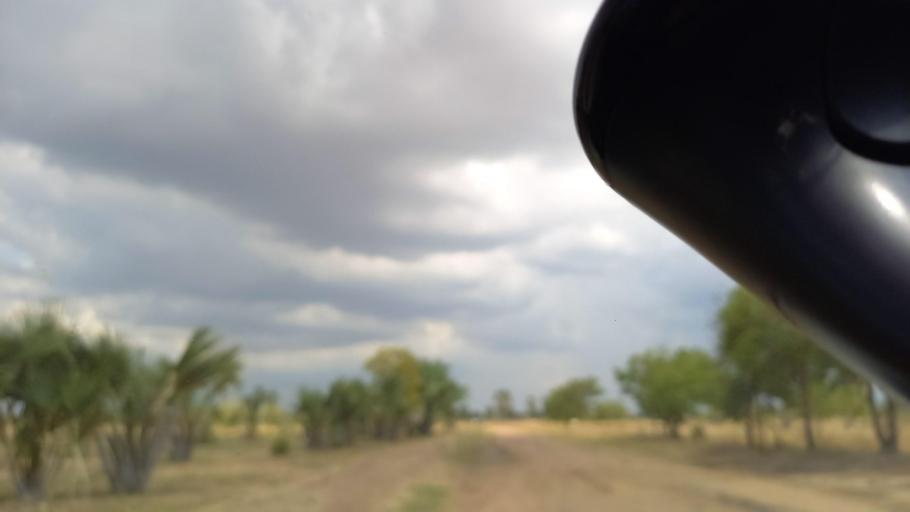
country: ZM
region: Lusaka
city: Kafue
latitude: -15.8364
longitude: 28.0802
